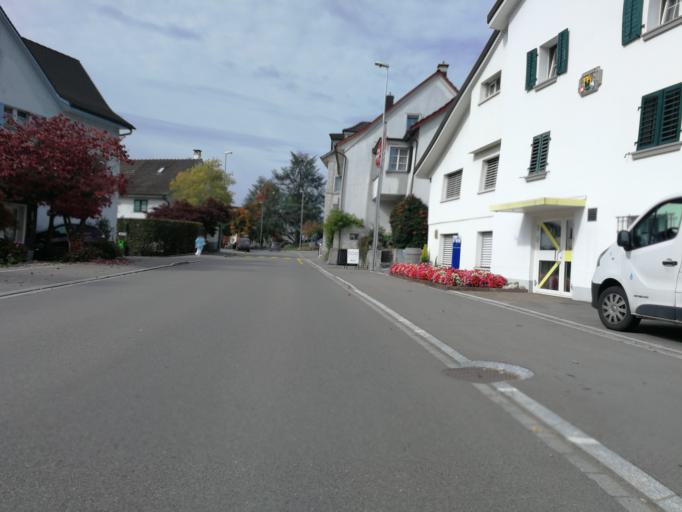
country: CH
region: Zurich
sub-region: Bezirk Meilen
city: Meilen
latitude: 47.2703
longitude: 8.6408
